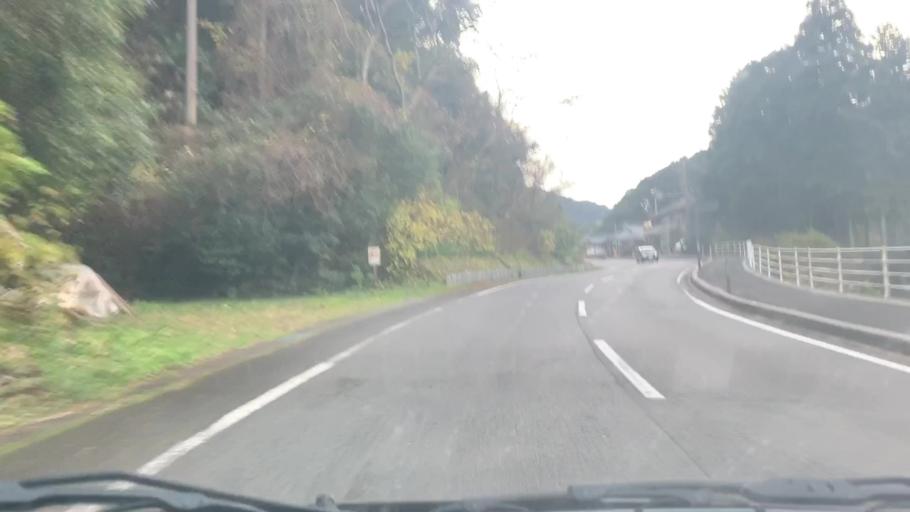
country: JP
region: Saga Prefecture
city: Kashima
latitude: 33.0219
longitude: 130.0672
